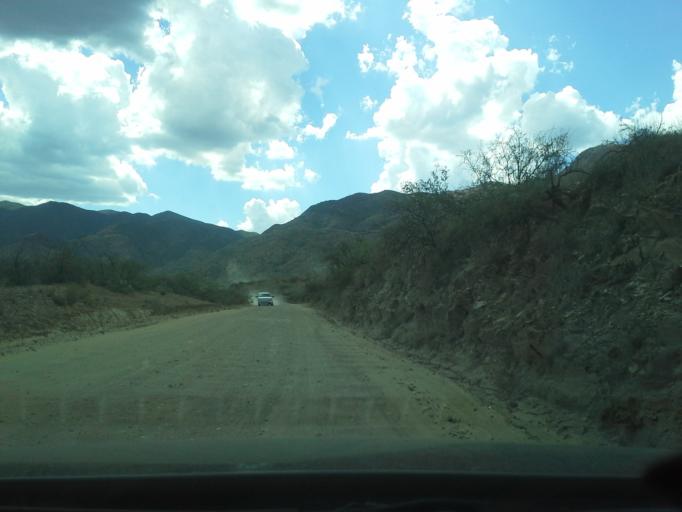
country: US
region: Arizona
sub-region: Yavapai County
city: Mayer
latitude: 34.2755
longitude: -112.2675
